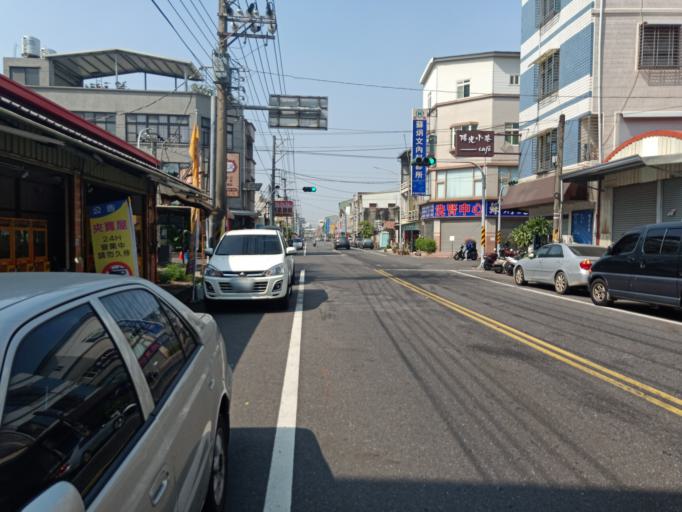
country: TW
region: Taiwan
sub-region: Tainan
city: Tainan
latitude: 23.1299
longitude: 120.2930
